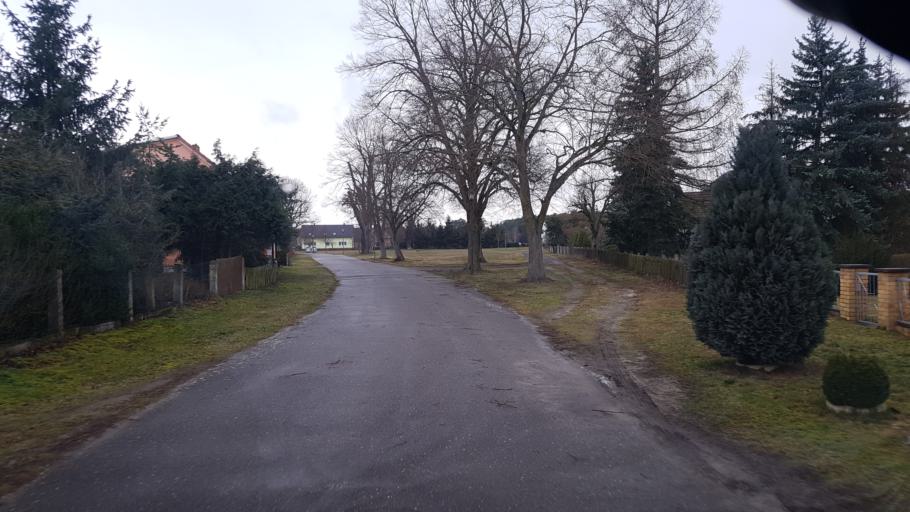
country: DE
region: Brandenburg
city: Sallgast
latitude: 51.6664
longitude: 13.8284
